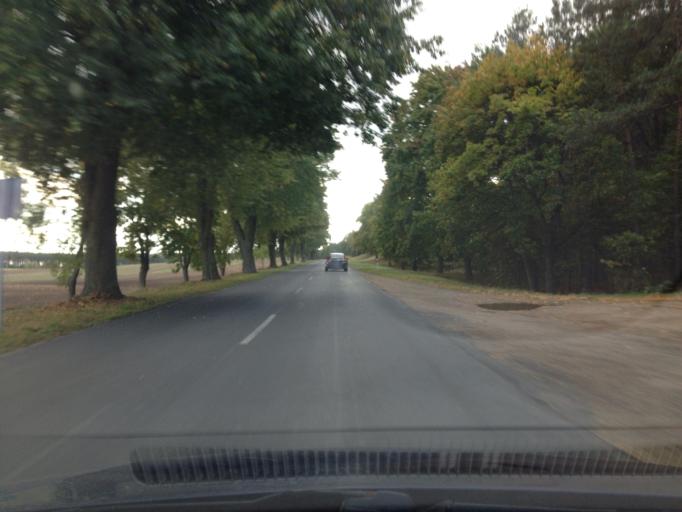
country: PL
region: Kujawsko-Pomorskie
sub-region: Powiat lipnowski
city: Chrostkowo
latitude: 52.9477
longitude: 19.2960
